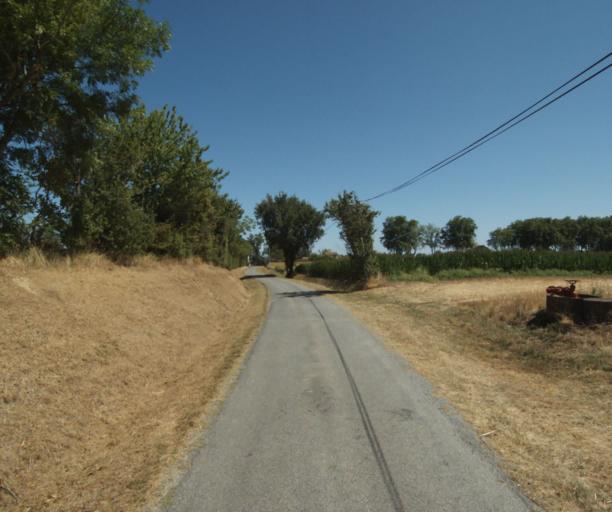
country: FR
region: Midi-Pyrenees
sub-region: Departement de la Haute-Garonne
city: Revel
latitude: 43.4984
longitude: 1.9561
